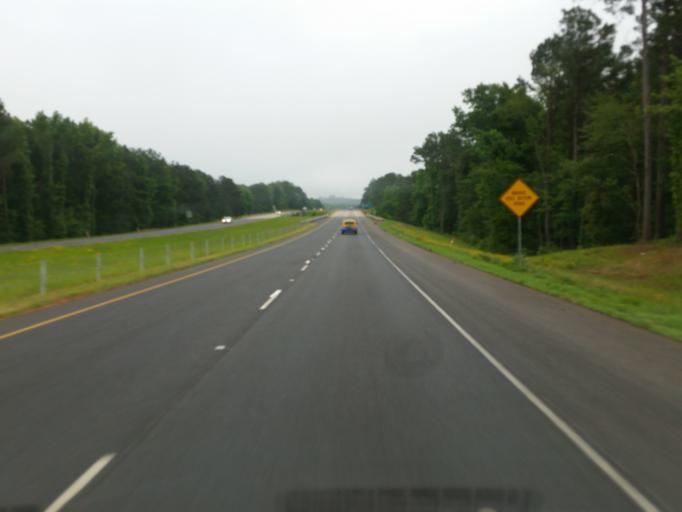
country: US
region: Louisiana
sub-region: Bienville Parish
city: Arcadia
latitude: 32.5633
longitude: -93.0667
